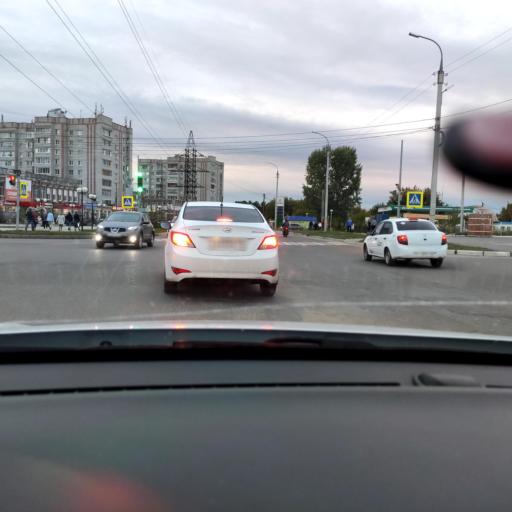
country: RU
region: Mariy-El
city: Volzhsk
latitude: 55.8676
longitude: 48.3506
